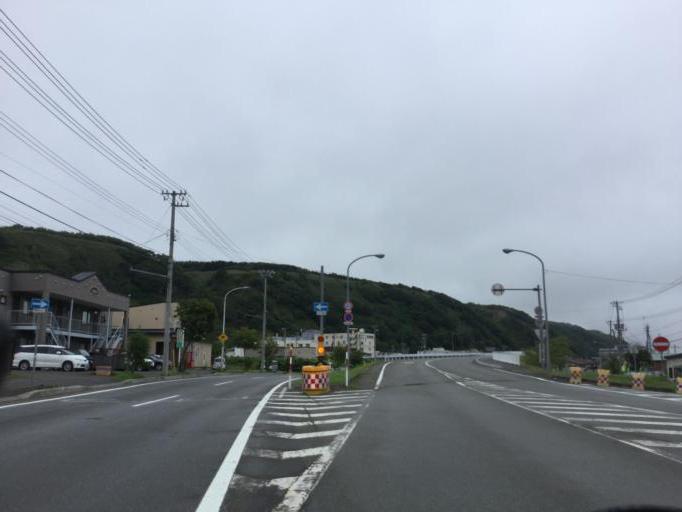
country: JP
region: Hokkaido
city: Wakkanai
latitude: 45.4038
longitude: 141.6766
